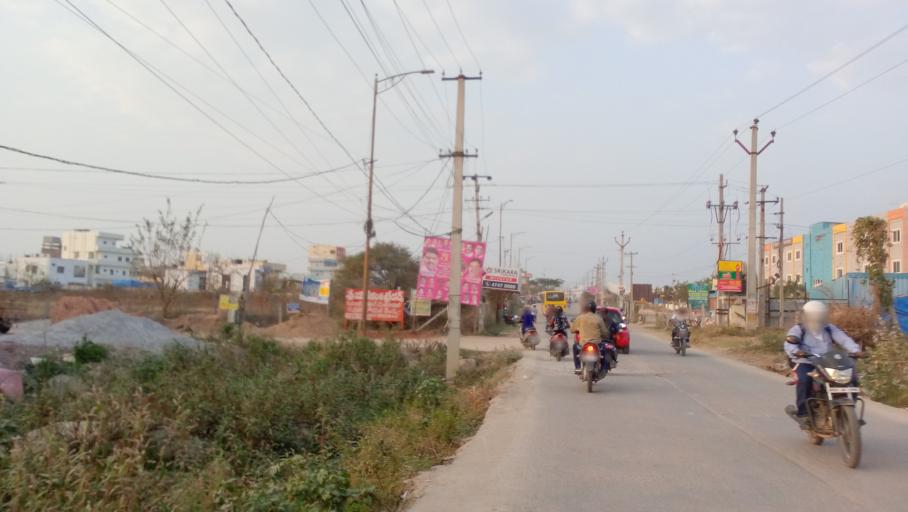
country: IN
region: Telangana
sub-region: Medak
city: Serilingampalle
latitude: 17.5149
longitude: 78.3190
